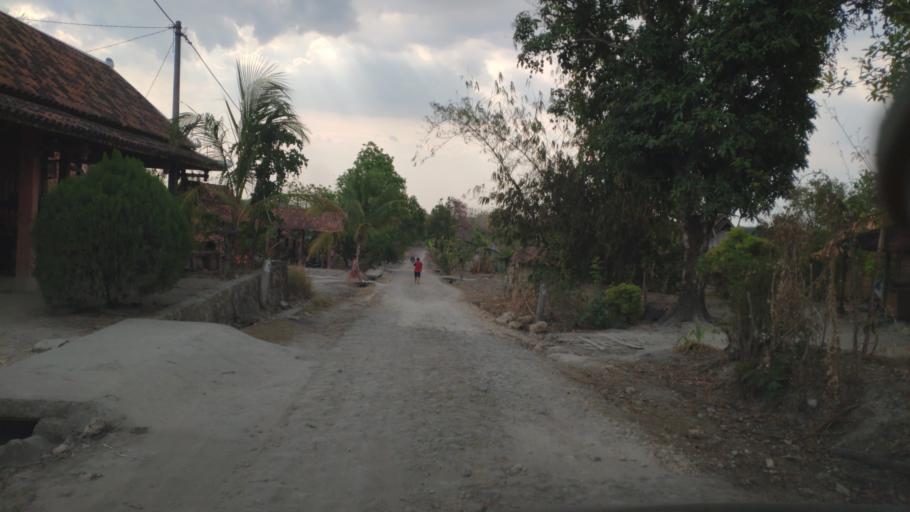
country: ID
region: Central Java
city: Randublatung
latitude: -7.2890
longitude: 111.3073
